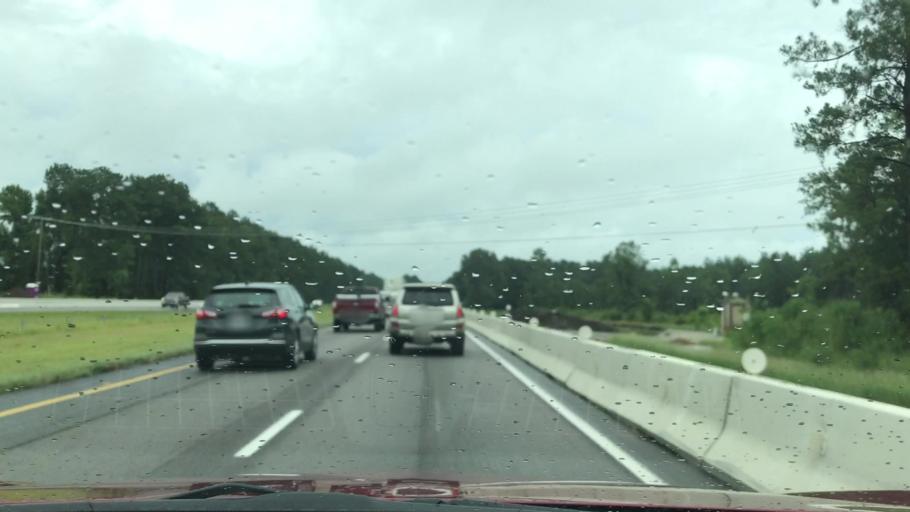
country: US
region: South Carolina
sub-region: Dorchester County
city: Ridgeville
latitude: 33.1146
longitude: -80.2663
